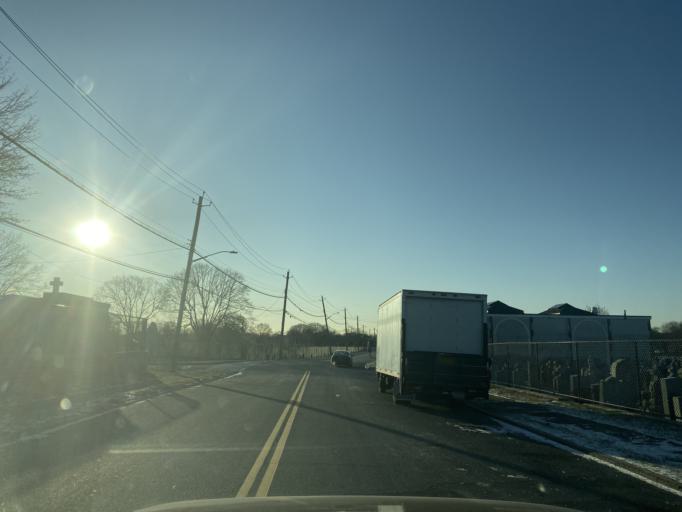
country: US
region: New York
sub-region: Bronx
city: The Bronx
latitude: 40.8343
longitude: -73.8356
